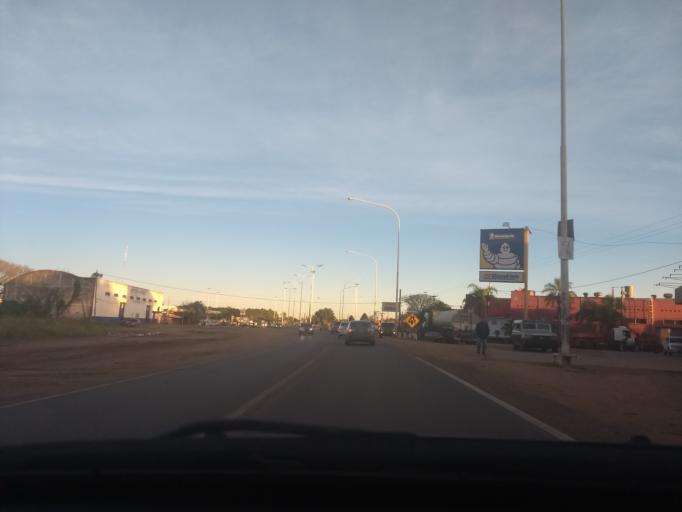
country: AR
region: Corrientes
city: Corrientes
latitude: -27.4812
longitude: -58.7836
